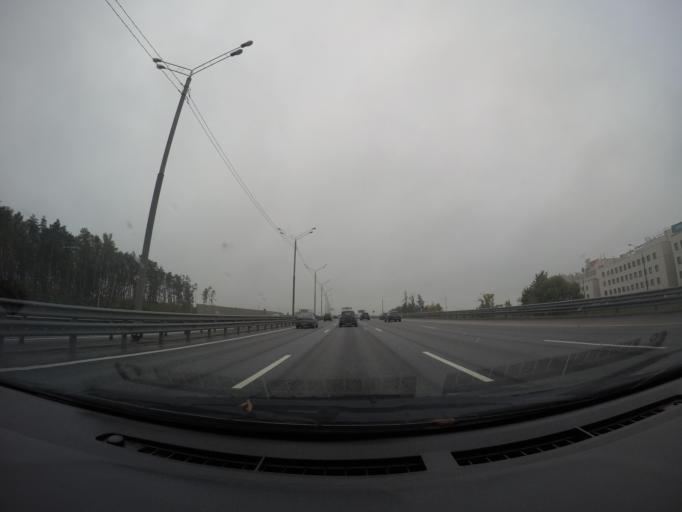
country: RU
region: Moskovskaya
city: Opalikha
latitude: 55.7843
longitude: 37.2441
